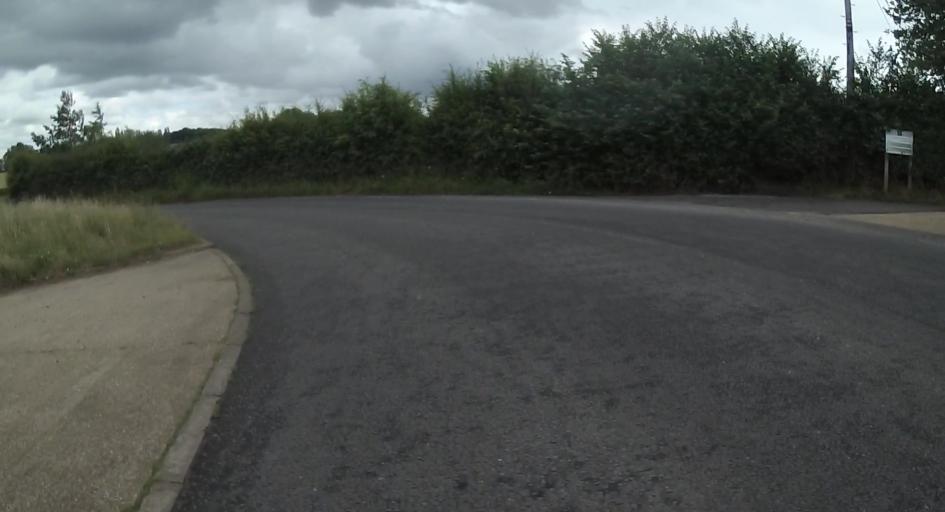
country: GB
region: England
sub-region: Surrey
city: Farnham
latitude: 51.2251
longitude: -0.8539
